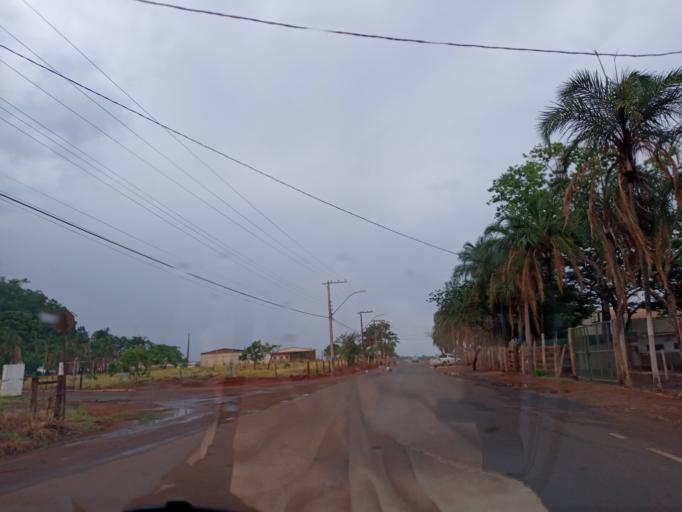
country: BR
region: Minas Gerais
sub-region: Ituiutaba
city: Ituiutaba
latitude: -18.9972
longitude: -49.4892
